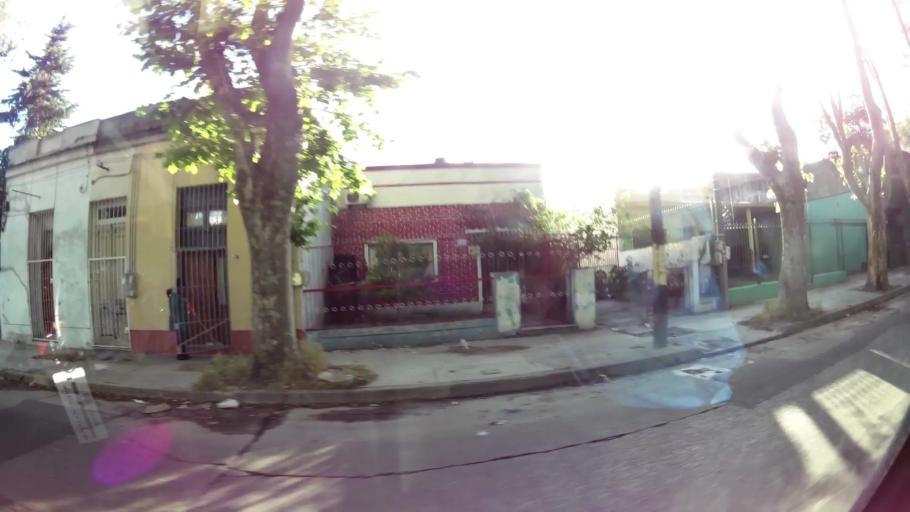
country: UY
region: Montevideo
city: Montevideo
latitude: -34.8801
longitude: -56.1384
